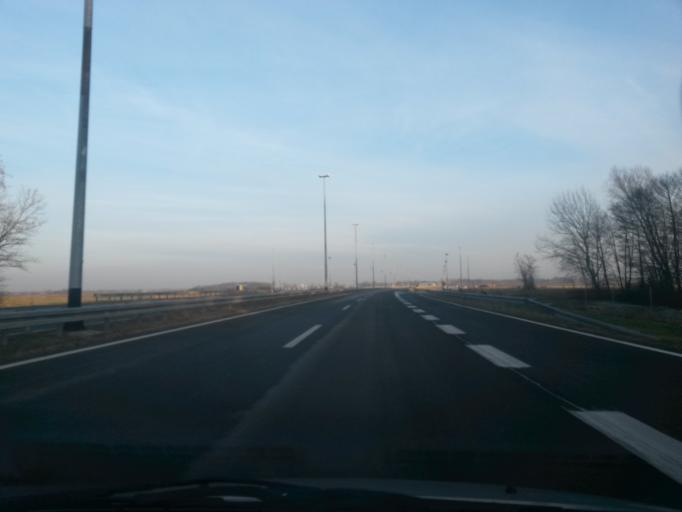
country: HR
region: Varazdinska
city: Jalzabet
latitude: 46.2842
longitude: 16.4517
